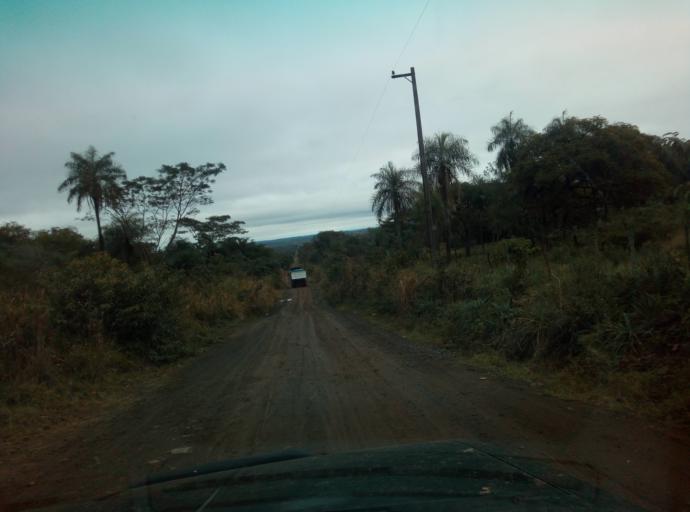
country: PY
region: Caaguazu
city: Carayao
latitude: -25.1902
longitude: -56.3751
